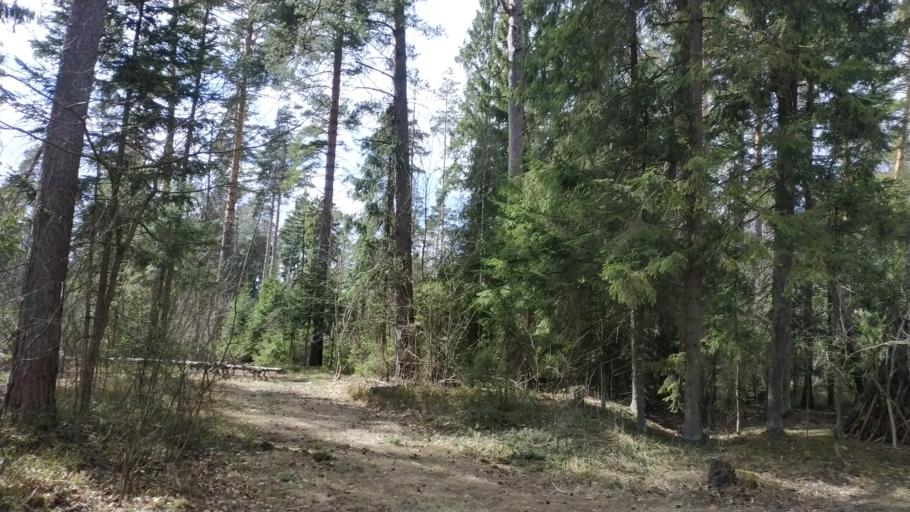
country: RU
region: Moskovskaya
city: Malyshevo
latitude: 55.5462
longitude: 38.3348
